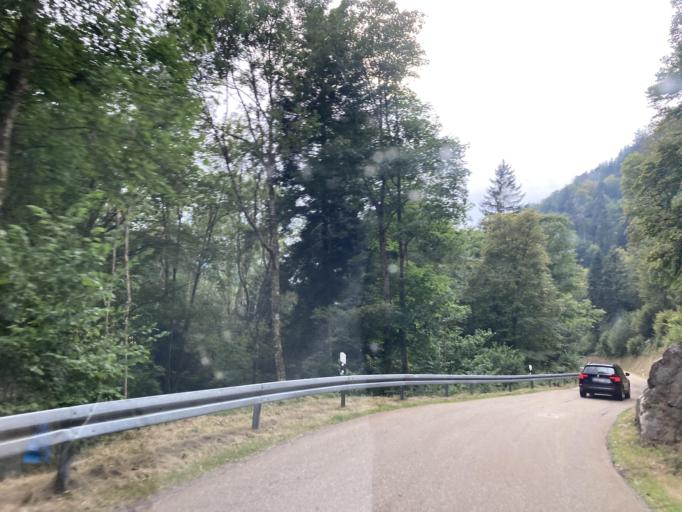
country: DE
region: Baden-Wuerttemberg
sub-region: Freiburg Region
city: Sulzburg
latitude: 47.8022
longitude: 7.7307
